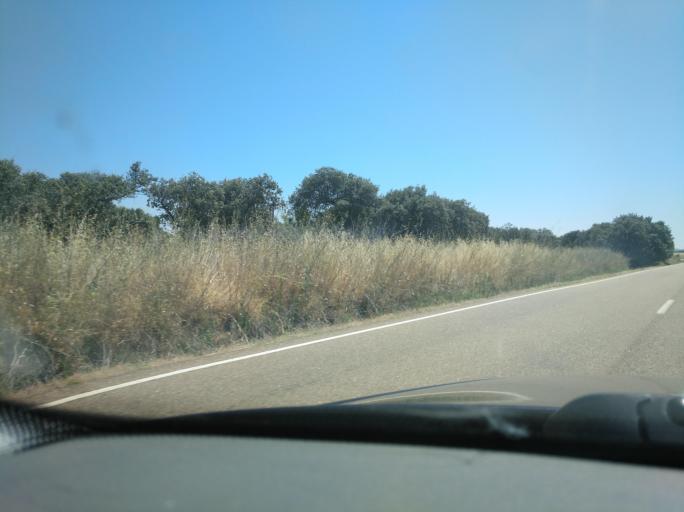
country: ES
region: Extremadura
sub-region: Provincia de Badajoz
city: Olivenza
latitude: 38.7081
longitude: -7.1815
